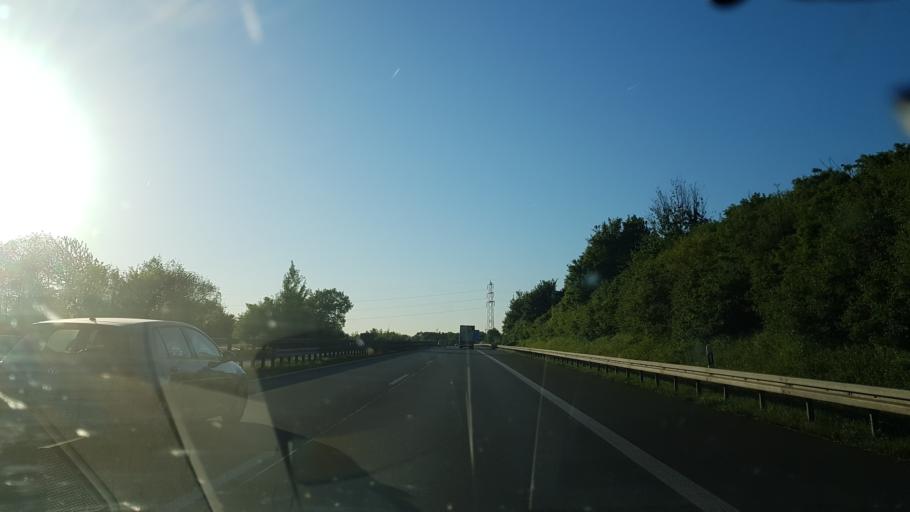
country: DE
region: North Rhine-Westphalia
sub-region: Regierungsbezirk Dusseldorf
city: Monchengladbach
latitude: 51.1866
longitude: 6.3896
